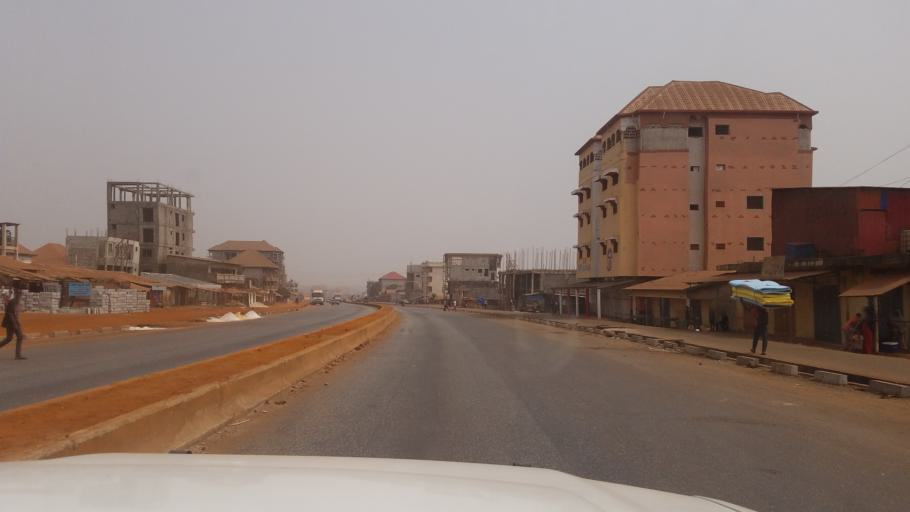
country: GN
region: Kindia
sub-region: Prefecture de Dubreka
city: Dubreka
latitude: 9.6851
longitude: -13.5216
